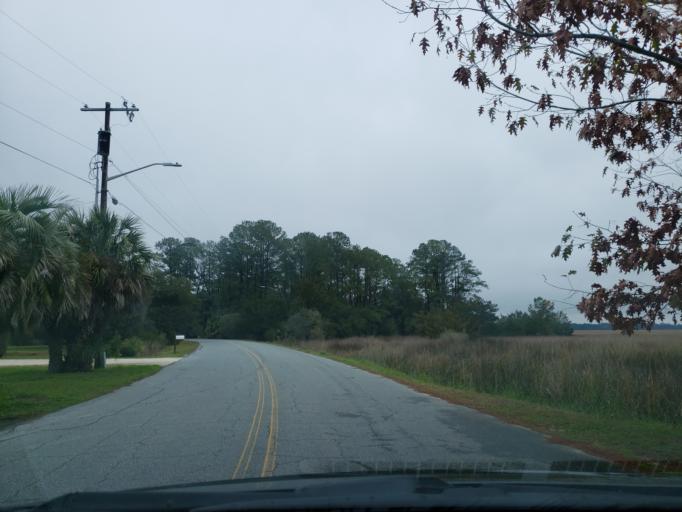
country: US
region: Georgia
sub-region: Chatham County
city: Georgetown
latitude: 31.9753
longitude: -81.1857
